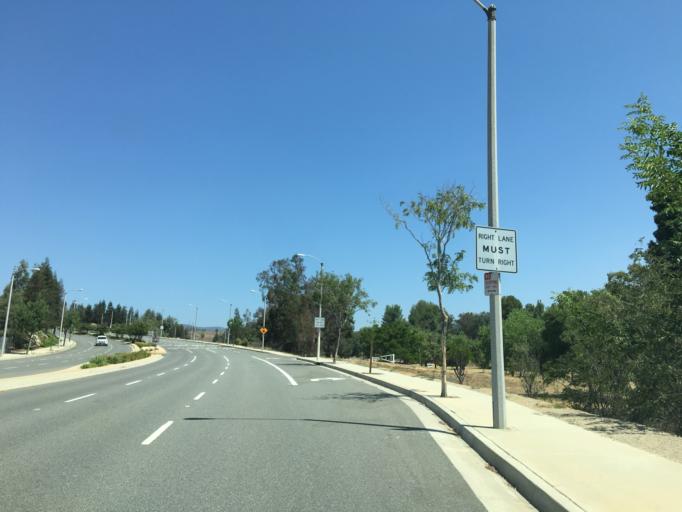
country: US
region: California
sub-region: Los Angeles County
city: Castaic
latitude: 34.4998
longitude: -118.6160
